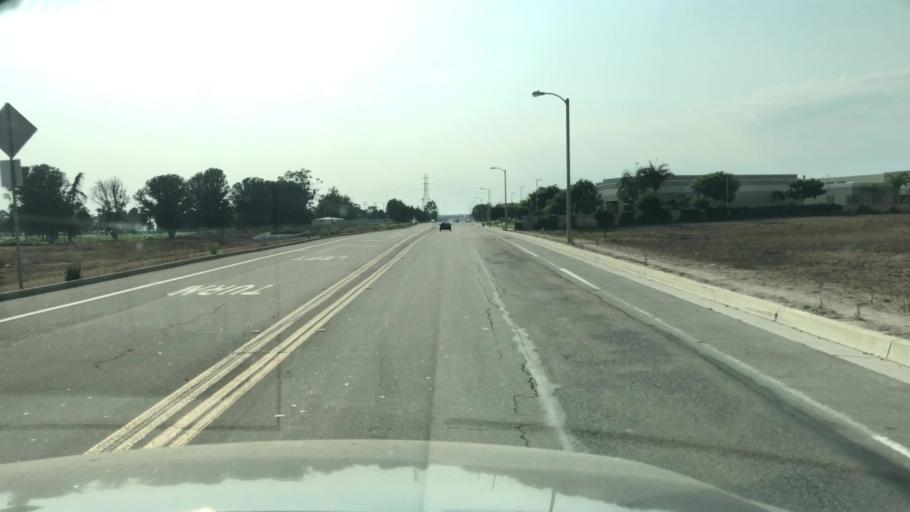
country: US
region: California
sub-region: Ventura County
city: El Rio
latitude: 34.2414
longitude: -119.2039
